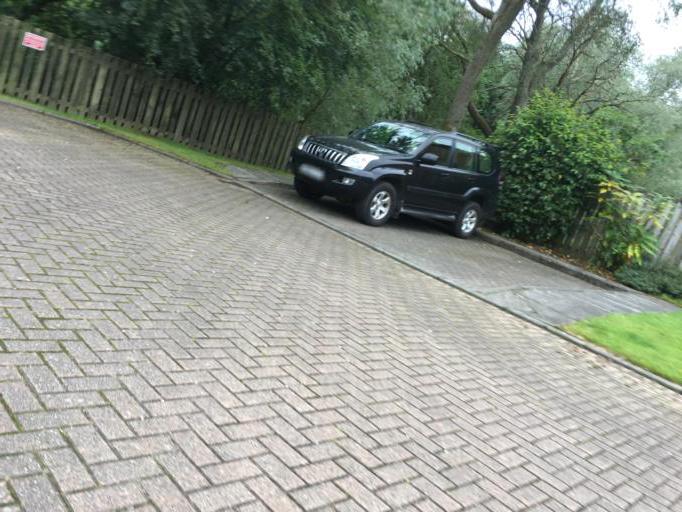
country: GB
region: Scotland
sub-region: West Lothian
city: Livingston
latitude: 55.8657
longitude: -3.5189
